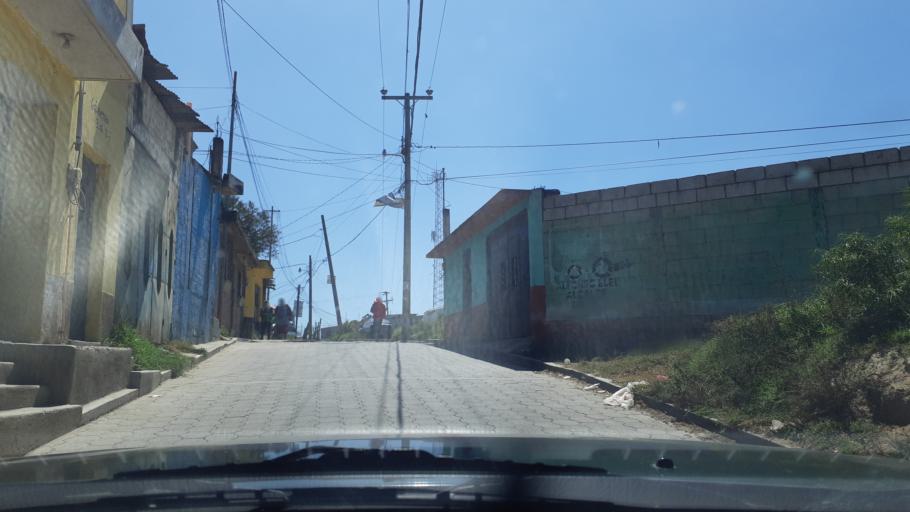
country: GT
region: Chimaltenango
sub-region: Municipio de Chimaltenango
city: Chimaltenango
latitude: 14.6678
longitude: -90.8430
